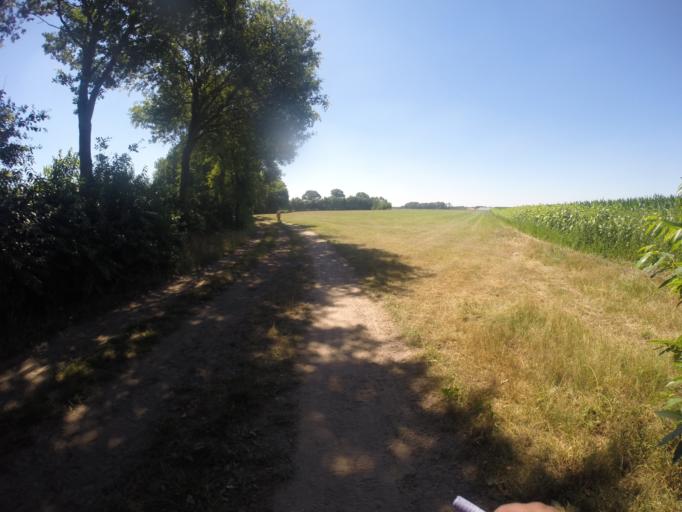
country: NL
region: Gelderland
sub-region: Gemeente Lochem
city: Barchem
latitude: 52.1294
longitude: 6.4292
